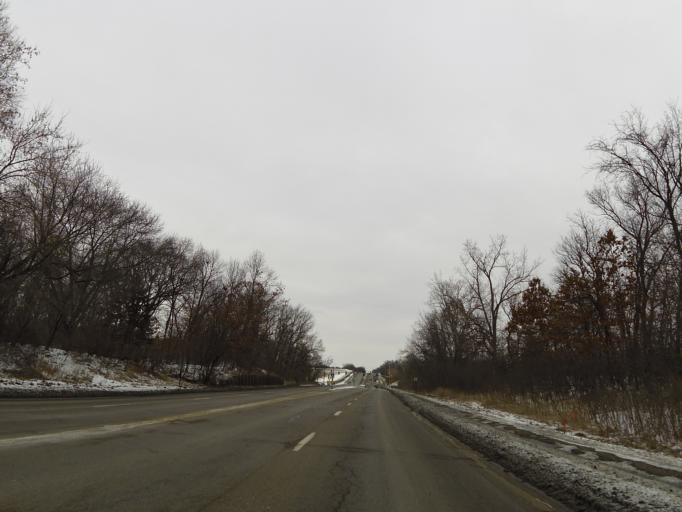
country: US
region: Minnesota
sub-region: Scott County
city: Savage
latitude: 44.8168
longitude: -93.3503
